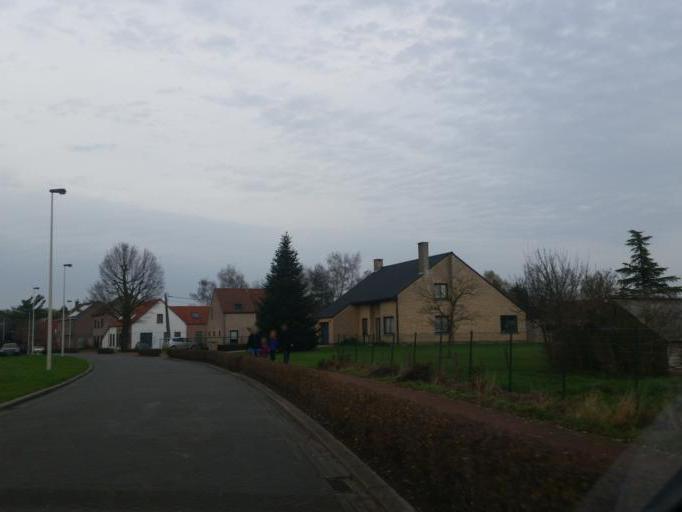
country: BE
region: Flanders
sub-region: Provincie Antwerpen
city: Duffel
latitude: 51.0839
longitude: 4.5100
